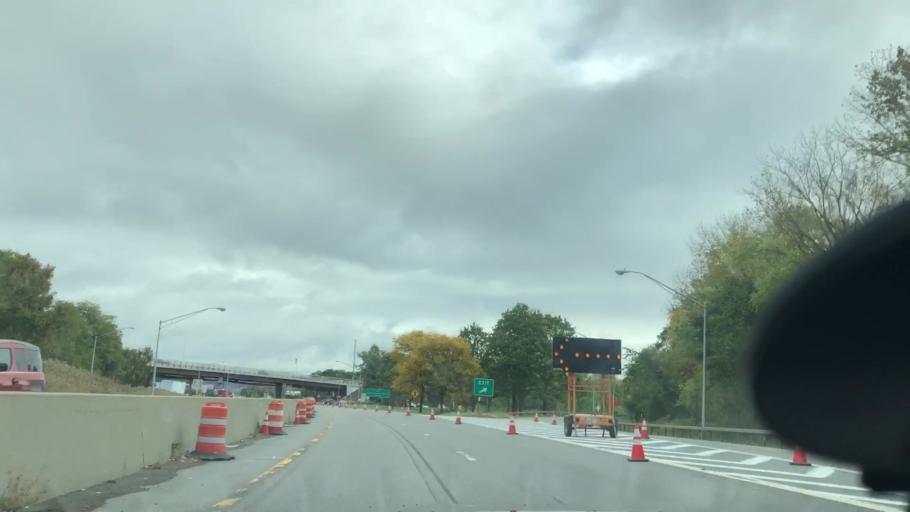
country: US
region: New York
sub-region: Oneida County
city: Yorkville
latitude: 43.0910
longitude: -75.2670
